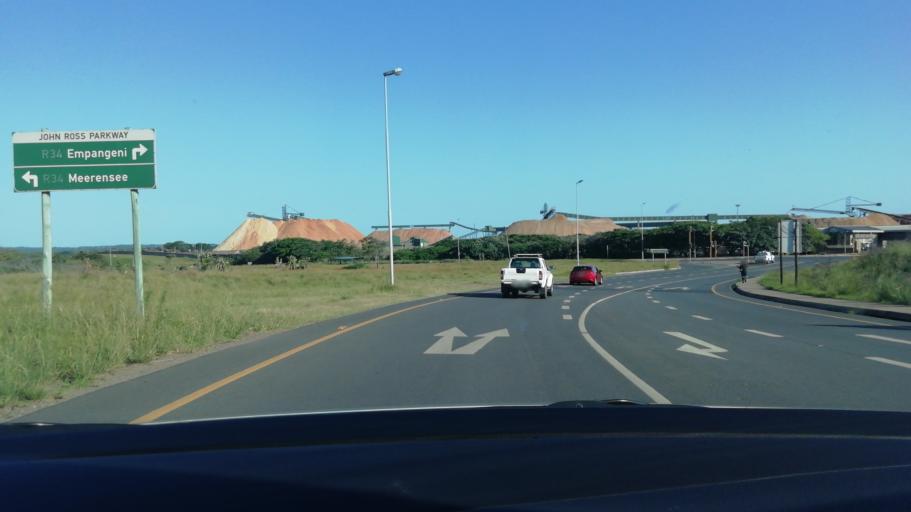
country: ZA
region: KwaZulu-Natal
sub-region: uThungulu District Municipality
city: Richards Bay
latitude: -28.7689
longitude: 32.0368
